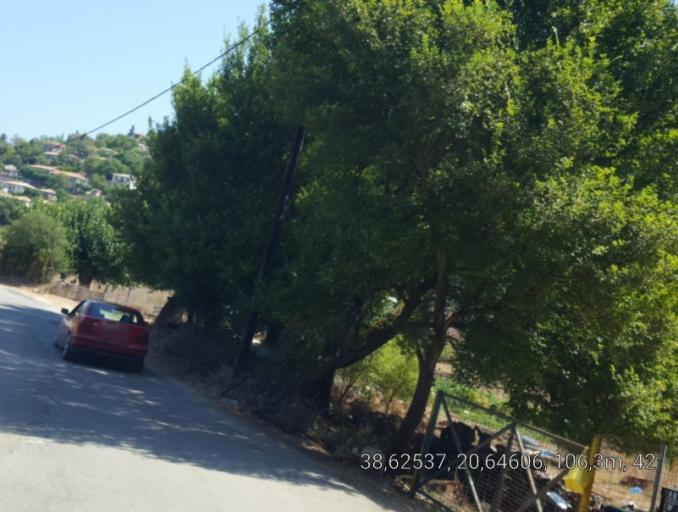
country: GR
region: Ionian Islands
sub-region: Lefkada
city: Nidri
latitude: 38.6253
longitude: 20.6461
